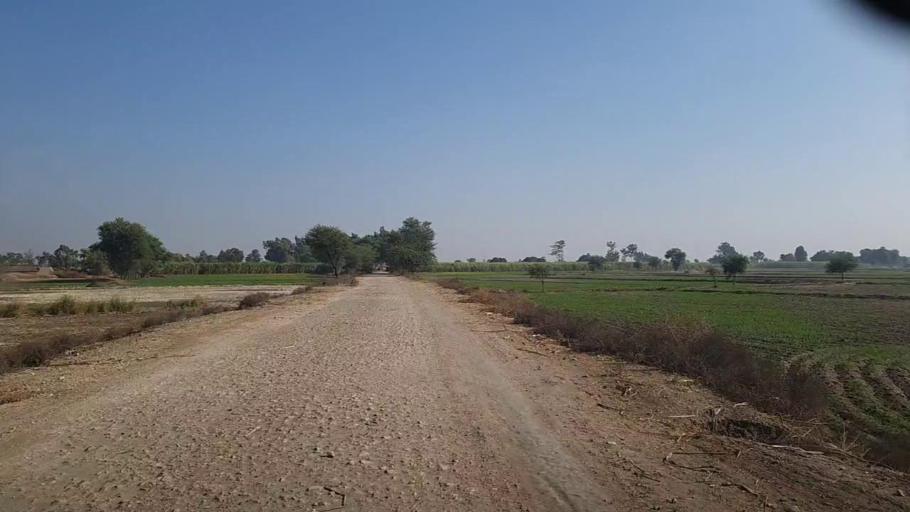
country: PK
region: Sindh
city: Darya Khan Marri
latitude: 26.6542
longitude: 68.3566
